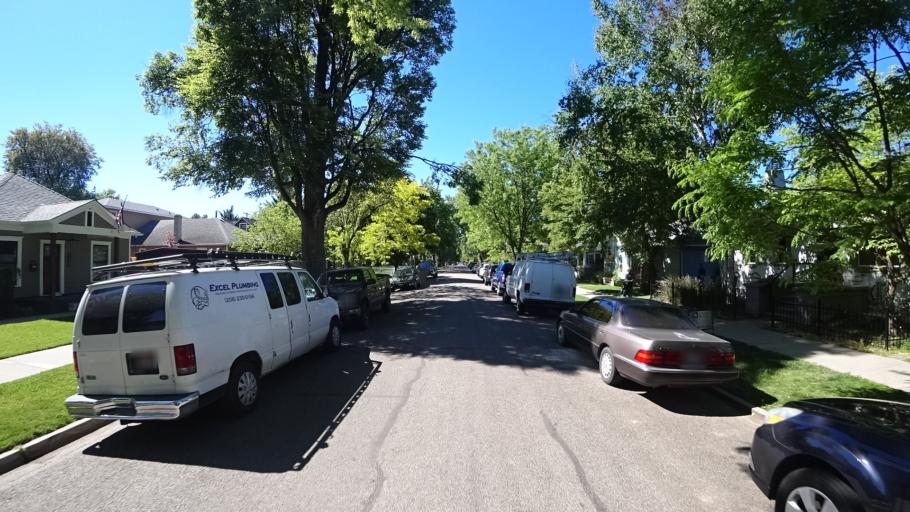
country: US
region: Idaho
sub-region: Ada County
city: Boise
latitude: 43.6328
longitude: -116.2134
